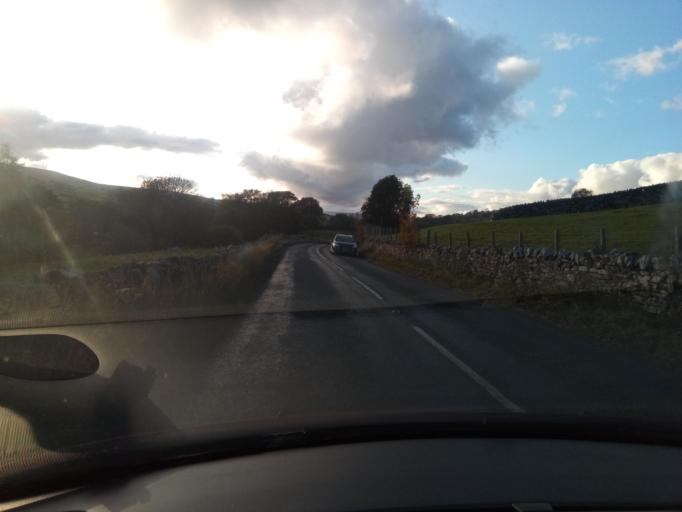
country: GB
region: England
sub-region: County Durham
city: Newbiggin
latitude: 54.7380
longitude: -2.1321
